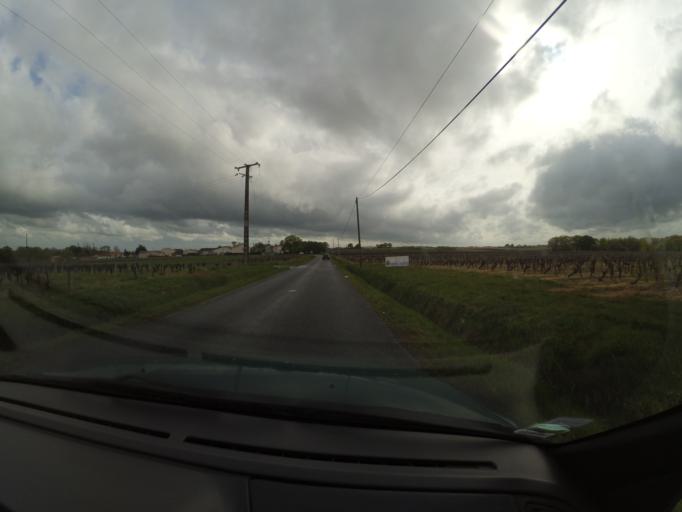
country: FR
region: Pays de la Loire
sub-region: Departement de la Loire-Atlantique
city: Monnieres
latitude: 47.1154
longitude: -1.3621
